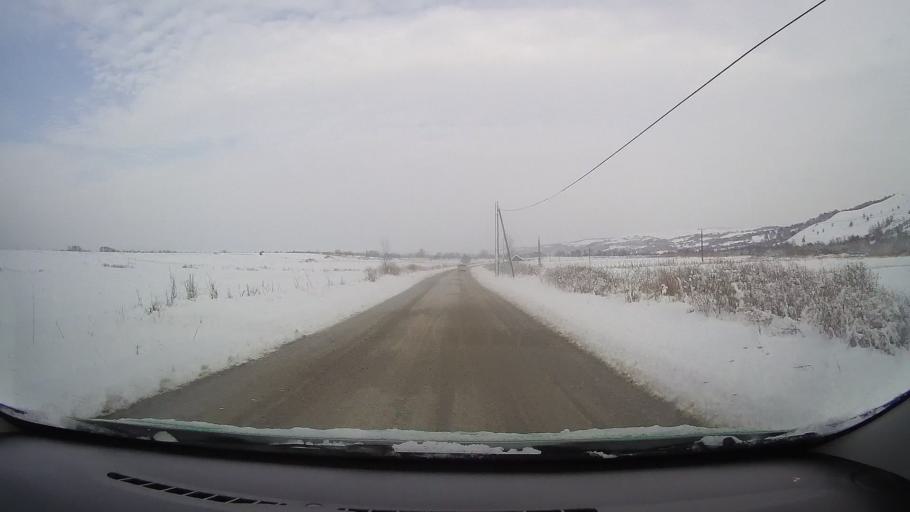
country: RO
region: Alba
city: Pianu de Sus
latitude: 45.9090
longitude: 23.4803
